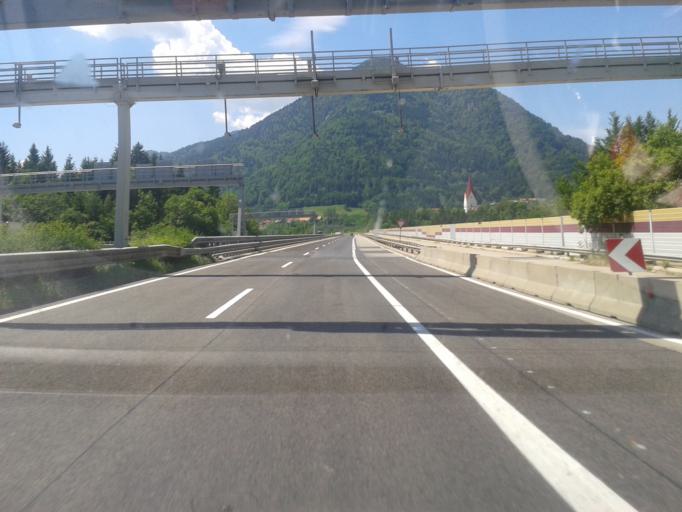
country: AT
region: Carinthia
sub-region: Politischer Bezirk Villach Land
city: Hohenthurn
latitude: 46.5383
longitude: 13.6607
